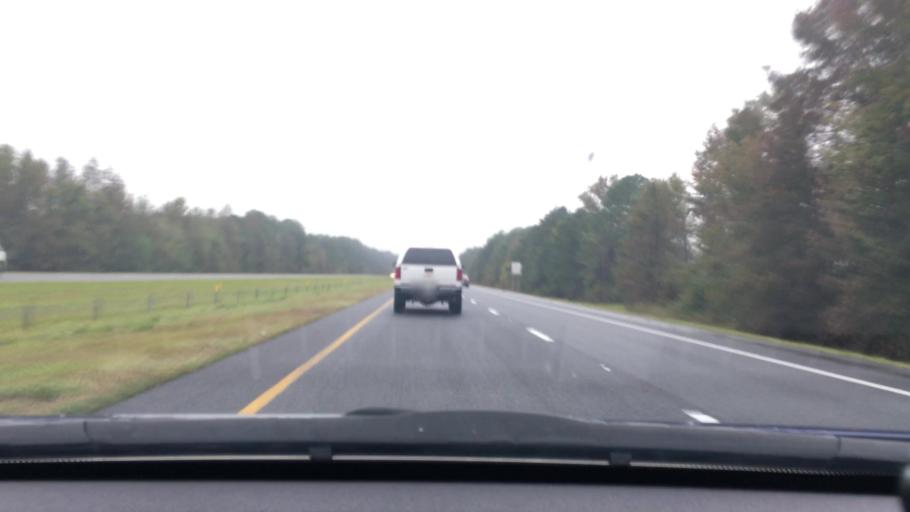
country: US
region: South Carolina
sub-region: Lee County
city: Bishopville
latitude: 34.1964
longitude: -80.1138
